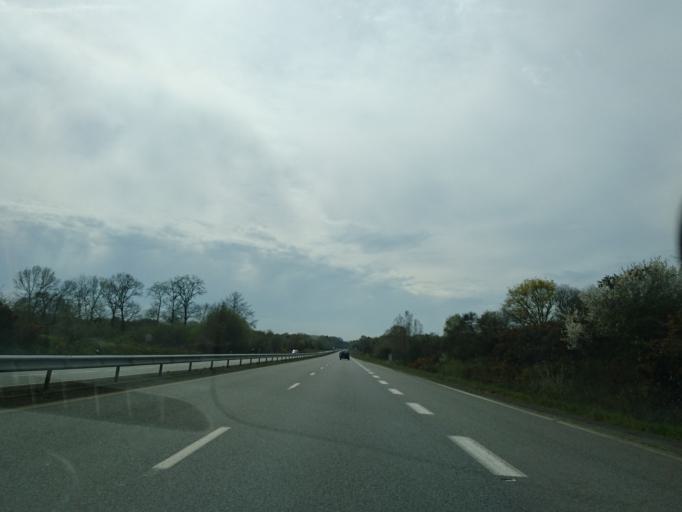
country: FR
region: Brittany
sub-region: Departement des Cotes-d'Armor
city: Trelivan
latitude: 48.4351
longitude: -2.1496
